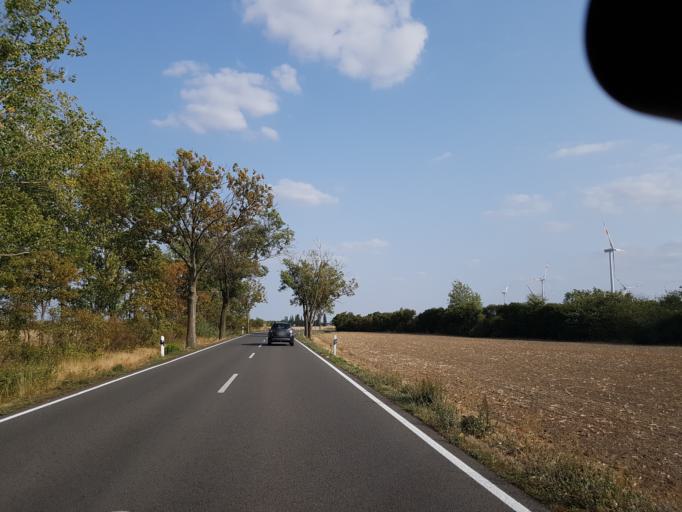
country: DE
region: Saxony-Anhalt
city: Muhlanger
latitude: 51.7817
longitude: 12.7172
